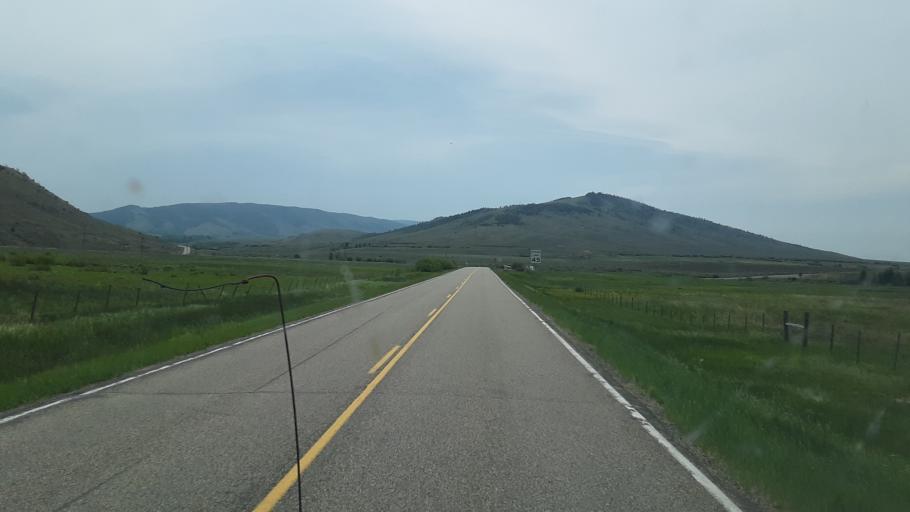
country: US
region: Colorado
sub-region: Jackson County
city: Walden
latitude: 40.9168
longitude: -106.2968
